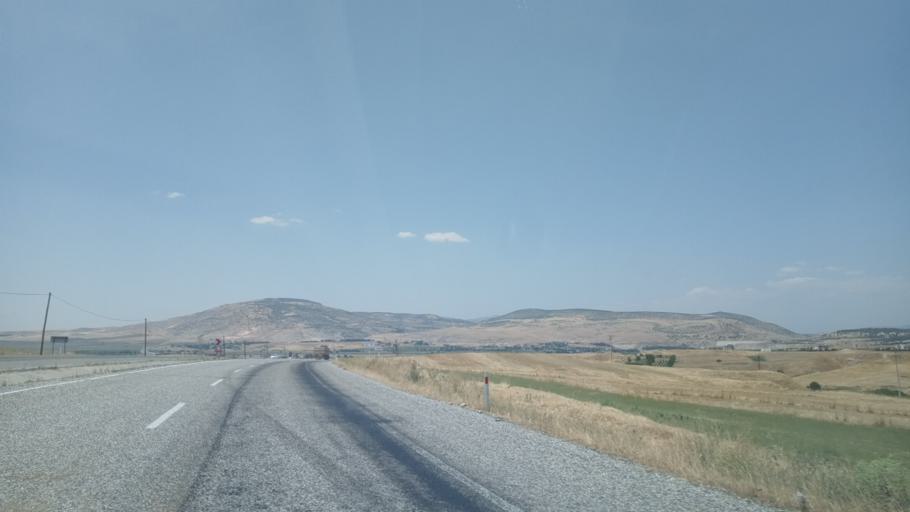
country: TR
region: Diyarbakir
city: Malabadi
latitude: 38.1340
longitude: 41.2435
